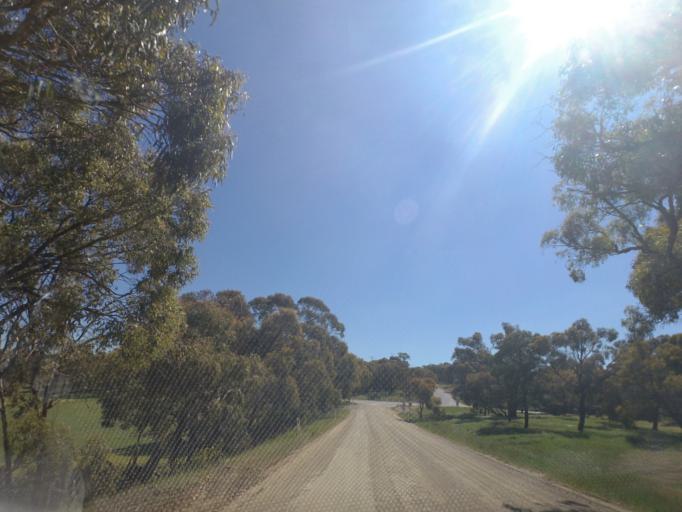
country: AU
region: Victoria
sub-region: Whittlesea
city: Whittlesea
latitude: -37.4005
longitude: 144.9535
